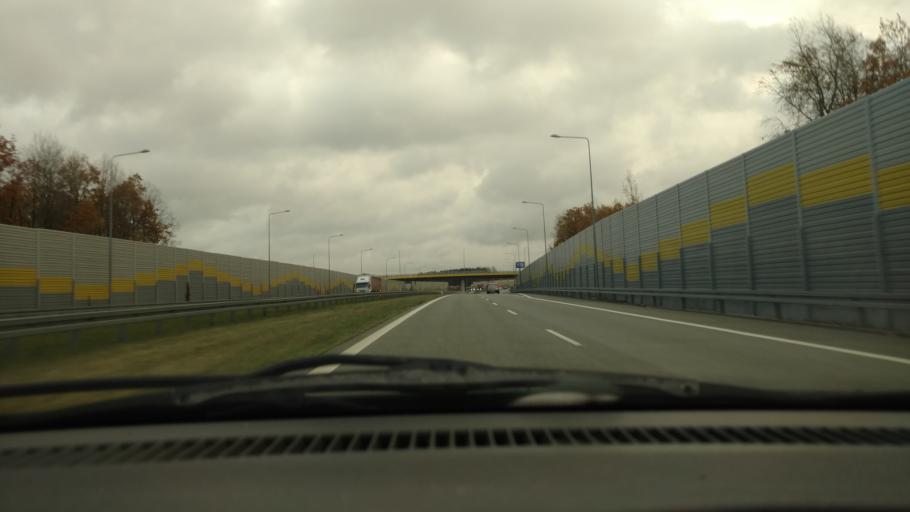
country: PL
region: Lodz Voivodeship
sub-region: Powiat pabianicki
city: Ksawerow
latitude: 51.6328
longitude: 19.4300
